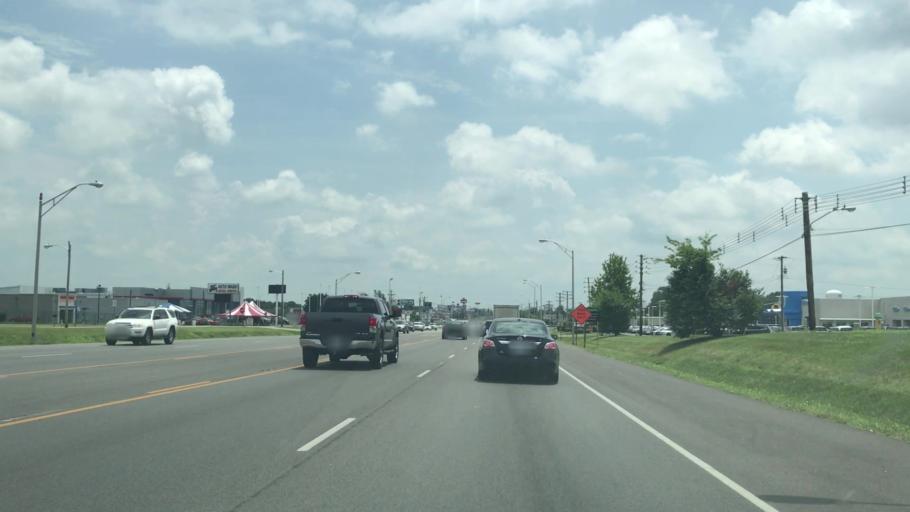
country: US
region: Kentucky
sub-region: Warren County
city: Bowling Green
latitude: 36.9570
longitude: -86.4281
